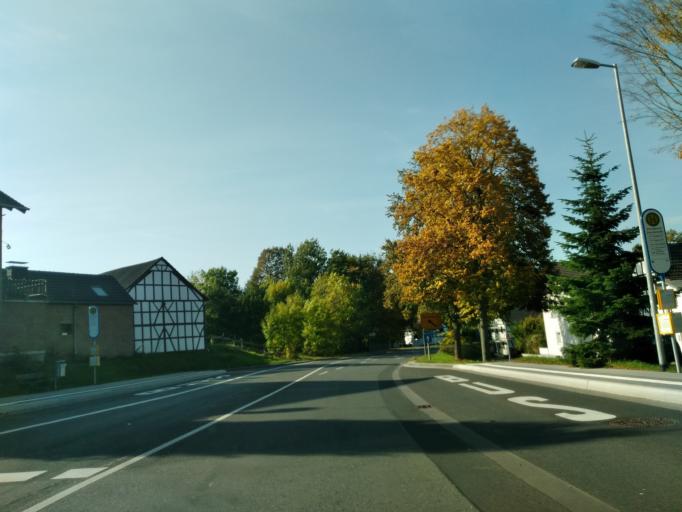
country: DE
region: North Rhine-Westphalia
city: Sankt Augustin
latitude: 50.7485
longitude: 7.2233
